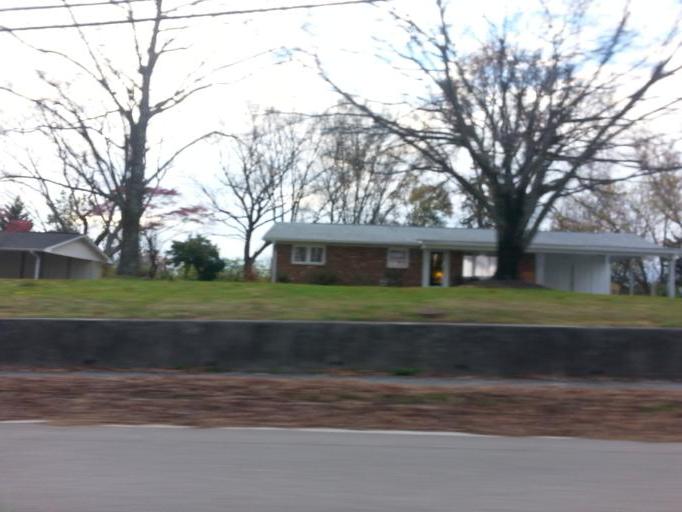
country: US
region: Tennessee
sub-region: Blount County
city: Louisville
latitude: 35.9226
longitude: -84.0419
